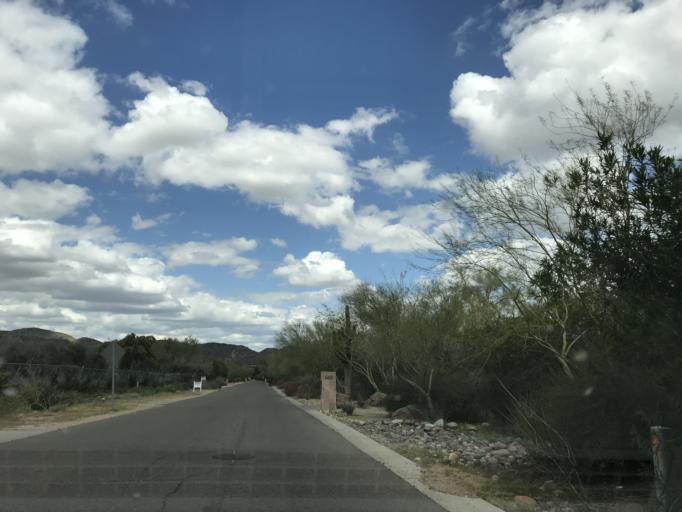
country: US
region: Arizona
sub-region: Maricopa County
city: Paradise Valley
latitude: 33.5182
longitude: -111.9454
